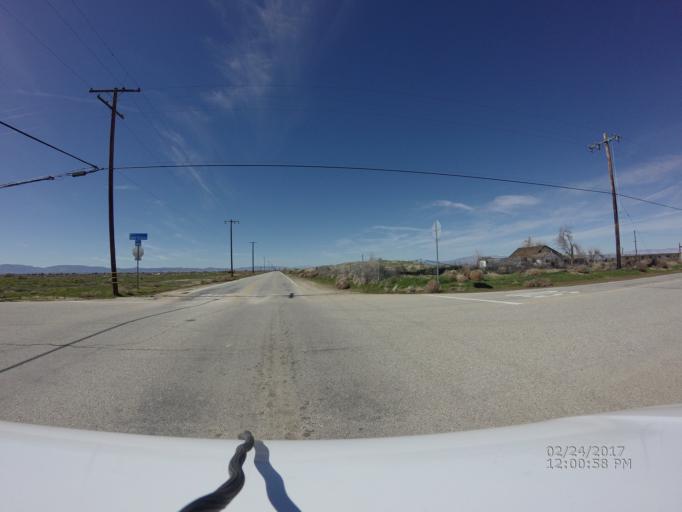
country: US
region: California
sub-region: Los Angeles County
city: Lancaster
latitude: 34.7192
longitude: -118.0234
